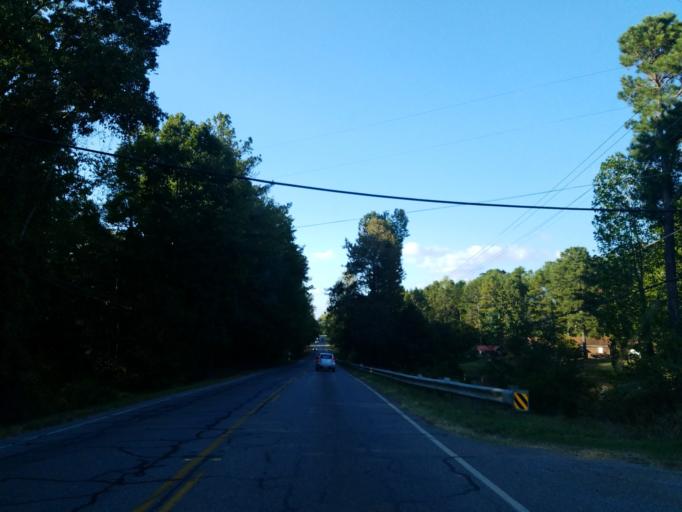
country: US
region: Georgia
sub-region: Bartow County
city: Cartersville
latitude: 34.0994
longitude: -84.8479
